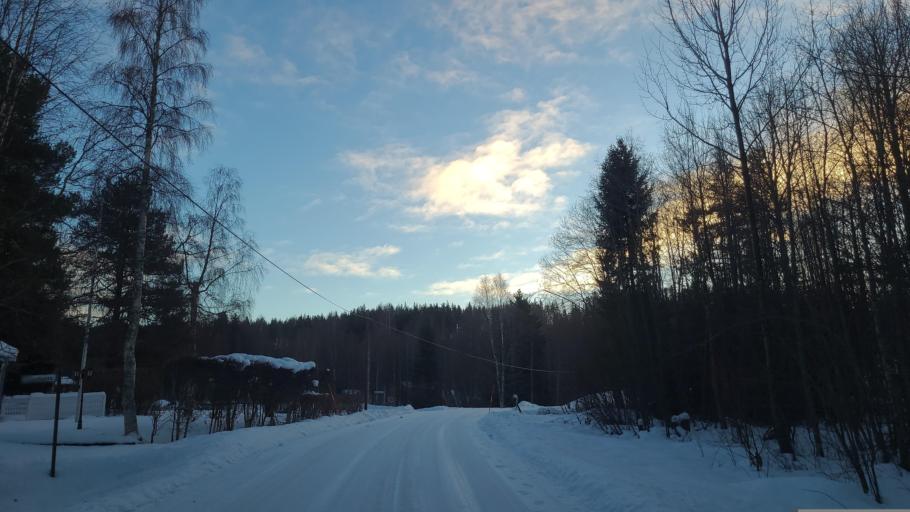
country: SE
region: Gaevleborg
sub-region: Bollnas Kommun
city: Kilafors
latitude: 61.3934
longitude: 16.6900
